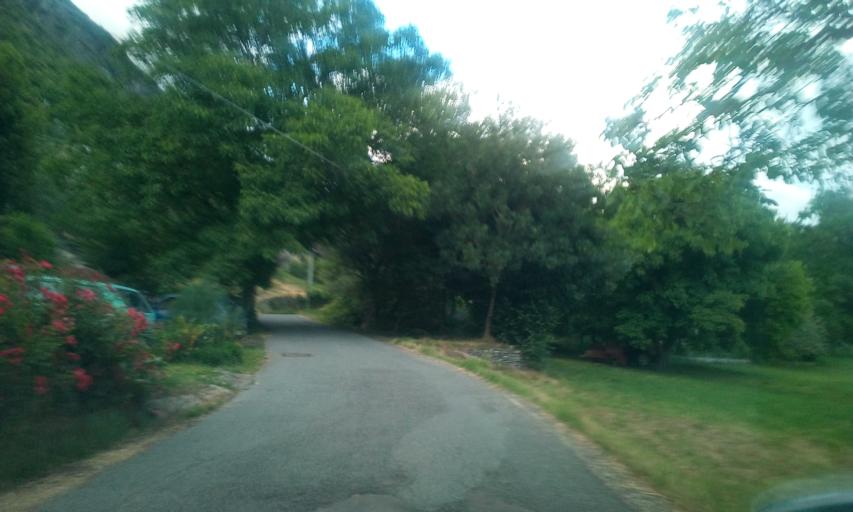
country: IT
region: Aosta Valley
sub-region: Valle d'Aosta
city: Saint-Vincent
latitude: 45.7581
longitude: 7.6349
